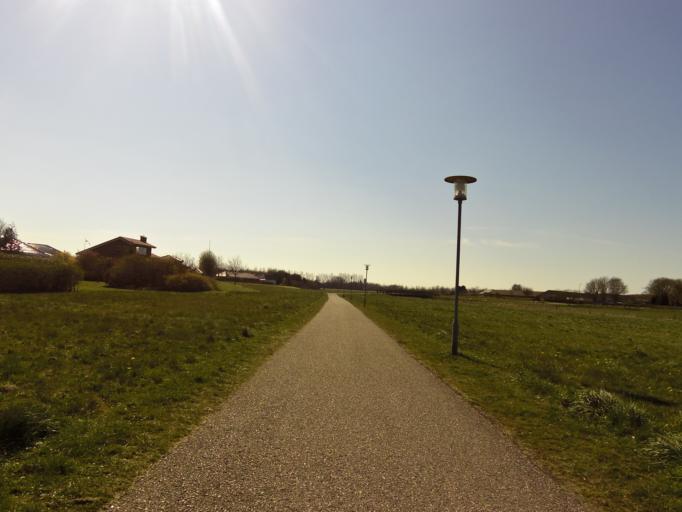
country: DK
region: South Denmark
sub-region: Esbjerg Kommune
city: Ribe
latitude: 55.3386
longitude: 8.7896
